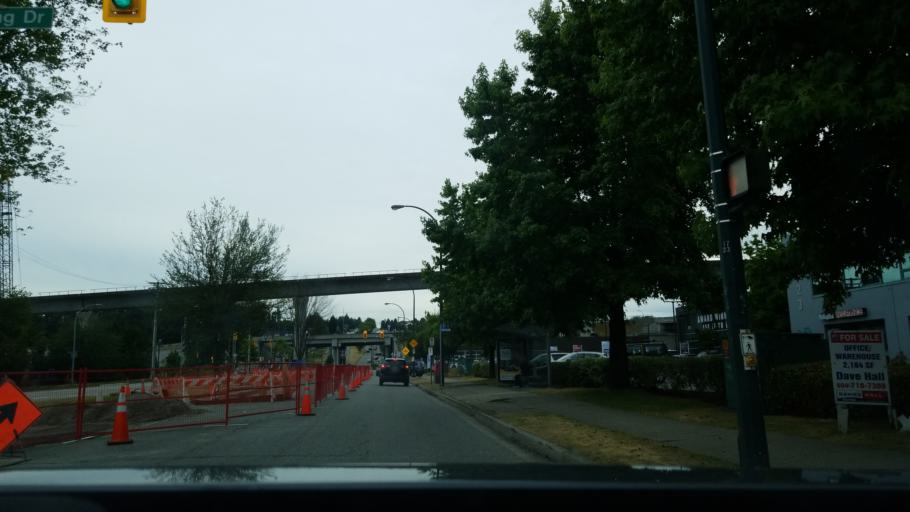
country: CA
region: British Columbia
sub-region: Fraser Valley Regional District
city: North Vancouver
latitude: 49.2636
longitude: -123.0238
